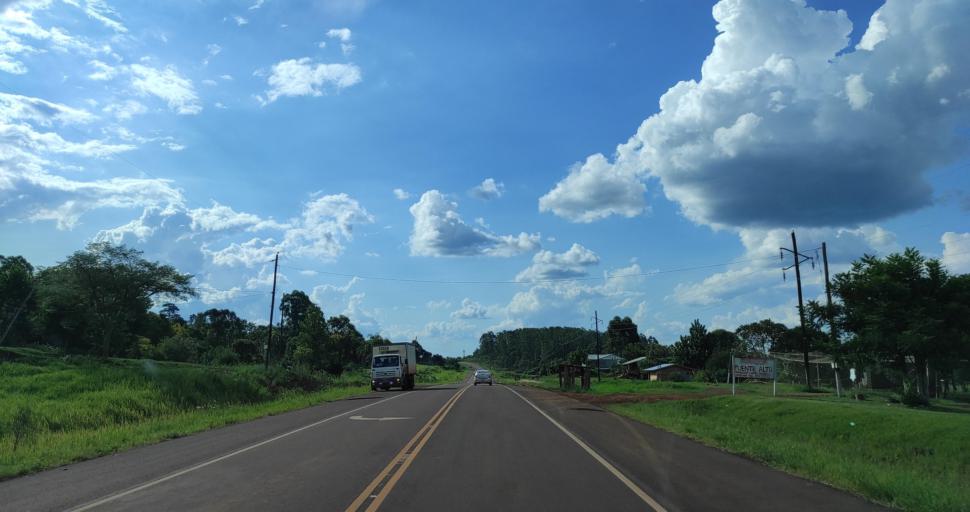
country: AR
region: Misiones
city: Bernardo de Irigoyen
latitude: -26.3845
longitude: -53.9138
